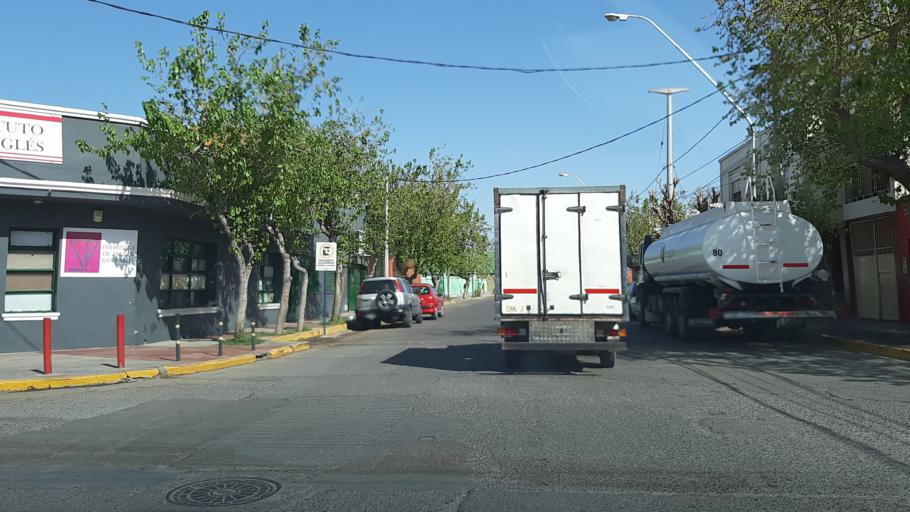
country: AR
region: San Juan
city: San Juan
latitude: -31.5301
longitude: -68.5193
